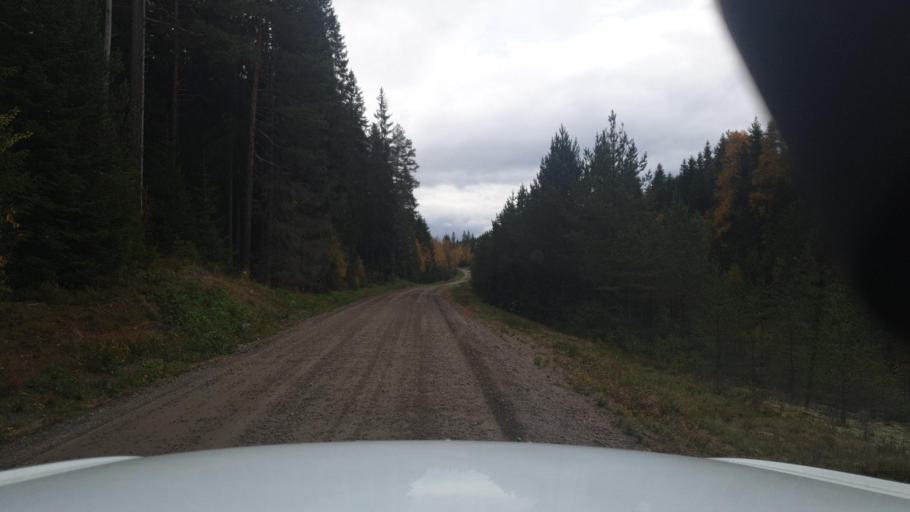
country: SE
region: Vaermland
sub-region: Eda Kommun
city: Charlottenberg
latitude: 60.0571
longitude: 12.5571
